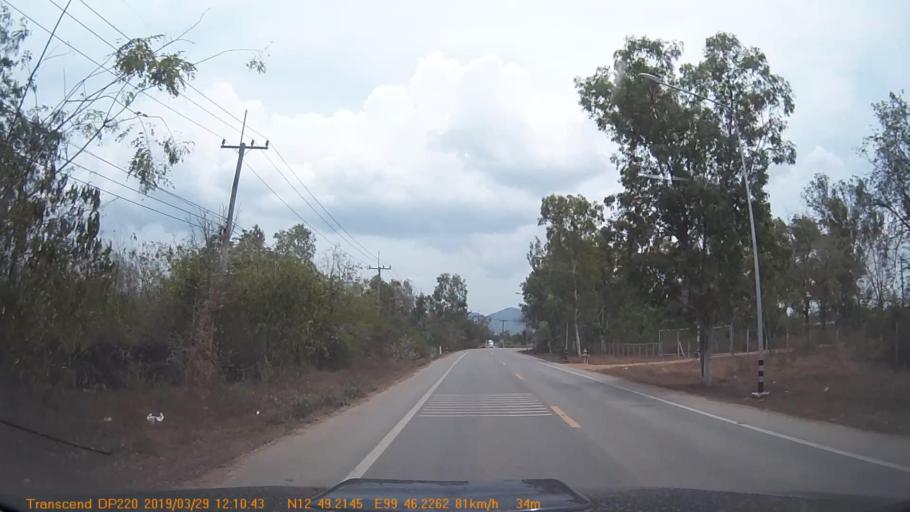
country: TH
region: Phetchaburi
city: Kaeng Krachan
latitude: 12.8202
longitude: 99.7706
